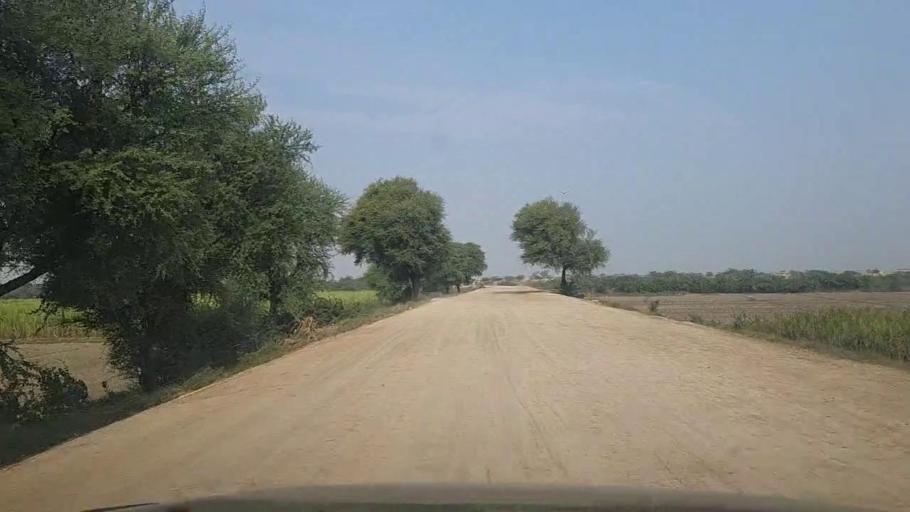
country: PK
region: Sindh
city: Bulri
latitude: 25.0308
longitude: 68.2801
